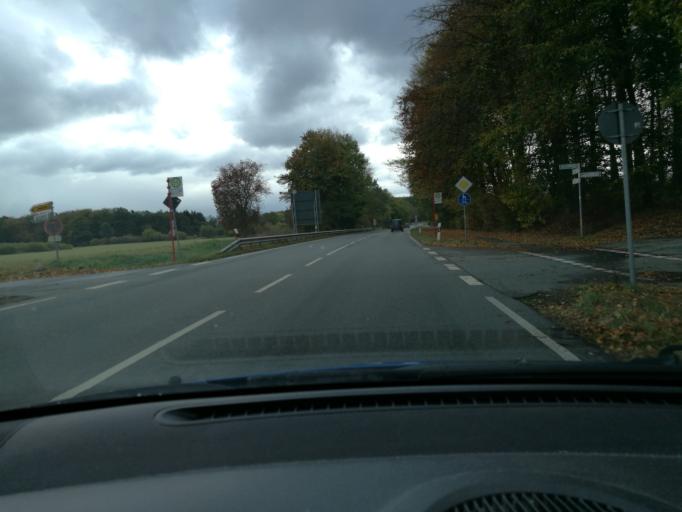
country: DE
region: Schleswig-Holstein
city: Gross Gronau
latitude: 53.7911
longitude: 10.7571
